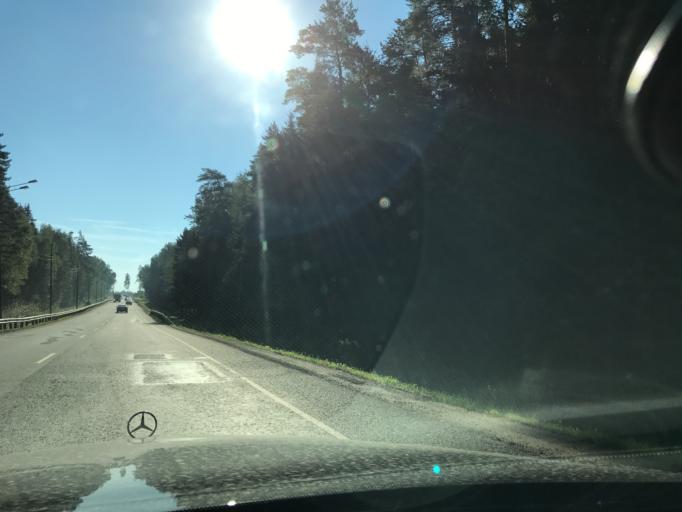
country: RU
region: Moskovskaya
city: Sverdlovskiy
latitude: 55.9280
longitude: 38.1884
